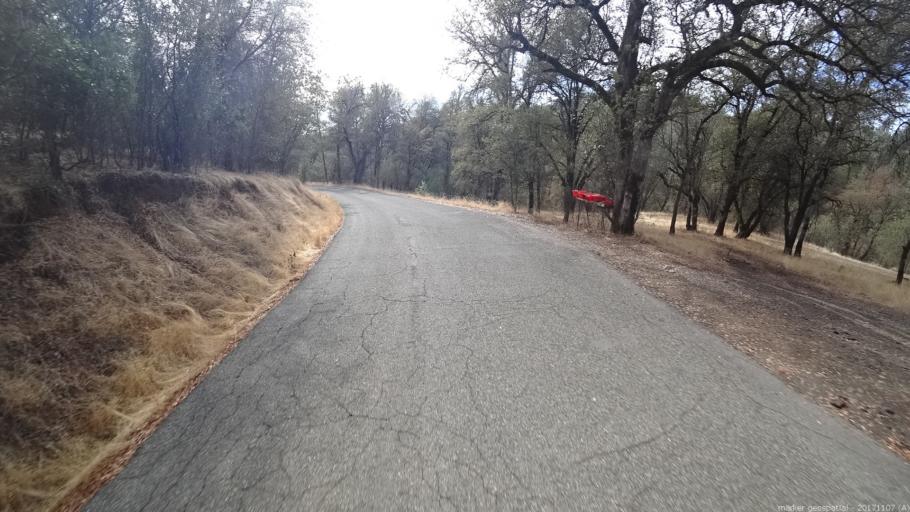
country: US
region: California
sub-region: Shasta County
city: Shasta
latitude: 40.5214
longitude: -122.5524
